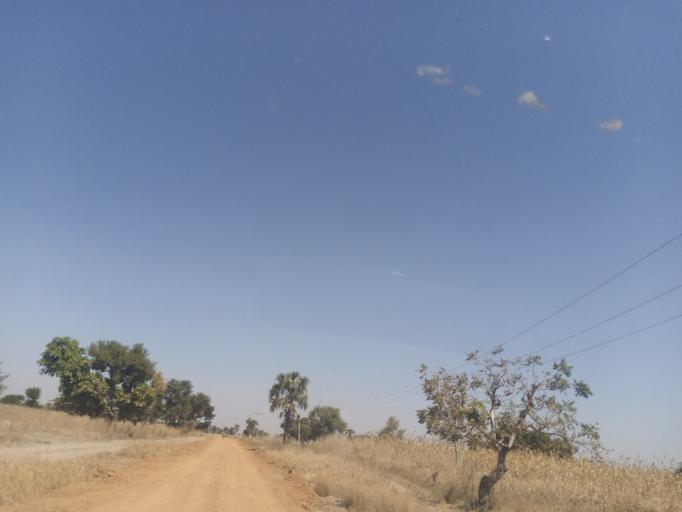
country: NG
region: Adamawa
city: Yola
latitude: 9.2987
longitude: 12.8878
